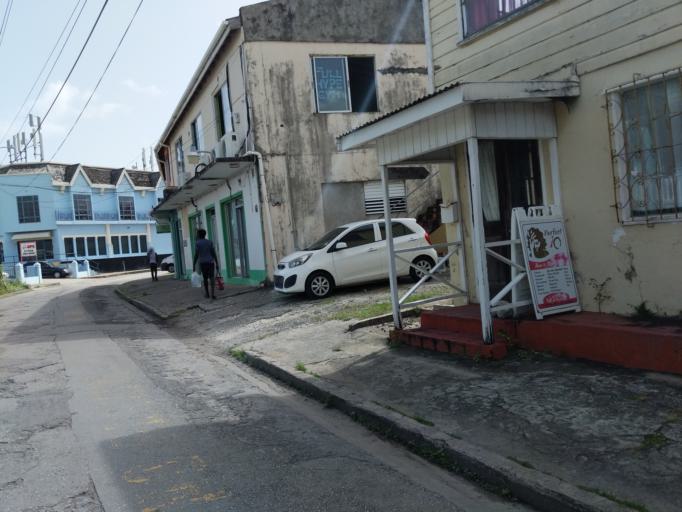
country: BB
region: Saint Peter
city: Speightstown
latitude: 13.2488
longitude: -59.6427
